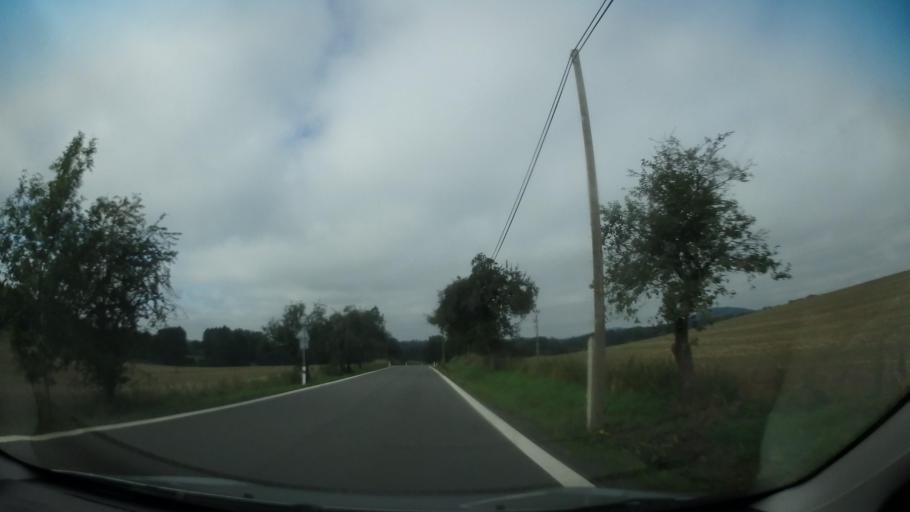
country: CZ
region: Central Bohemia
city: Bystrice
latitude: 49.7592
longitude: 14.6499
